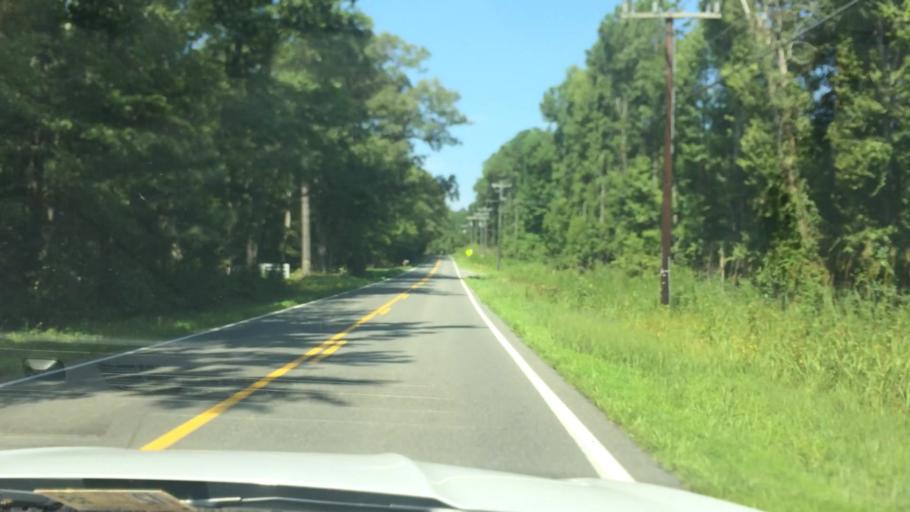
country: US
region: Virginia
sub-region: New Kent County
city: New Kent
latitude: 37.5265
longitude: -77.0185
